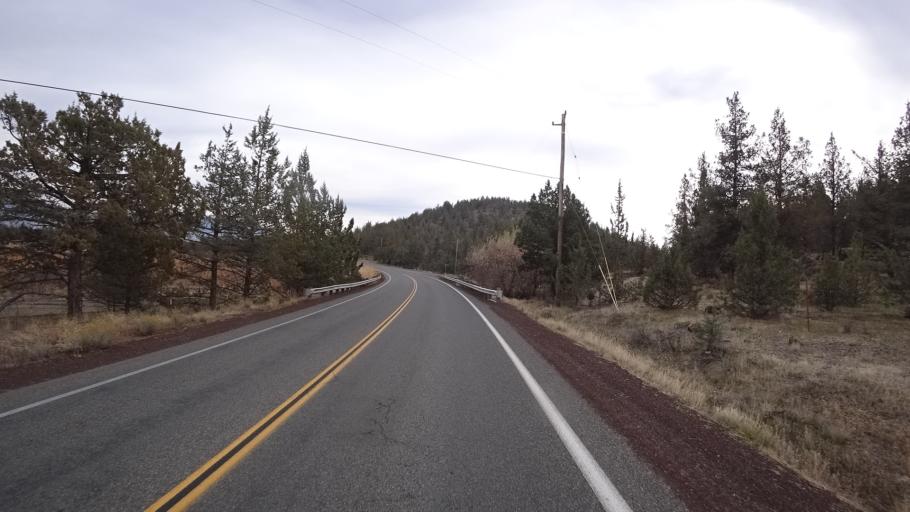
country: US
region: California
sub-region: Siskiyou County
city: Montague
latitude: 41.6353
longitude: -122.4536
